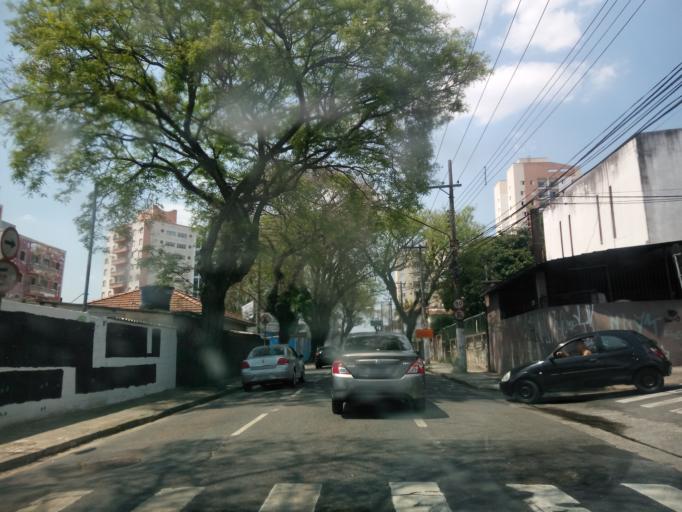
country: BR
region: Sao Paulo
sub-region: Sao Bernardo Do Campo
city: Sao Bernardo do Campo
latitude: -23.7055
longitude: -46.5561
